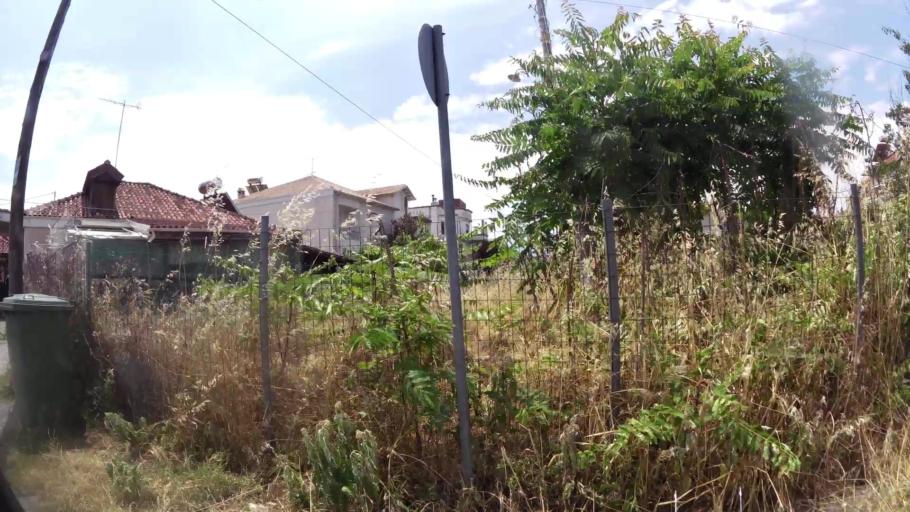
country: GR
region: Central Macedonia
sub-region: Nomos Pierias
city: Katerini
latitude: 40.2638
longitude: 22.5200
